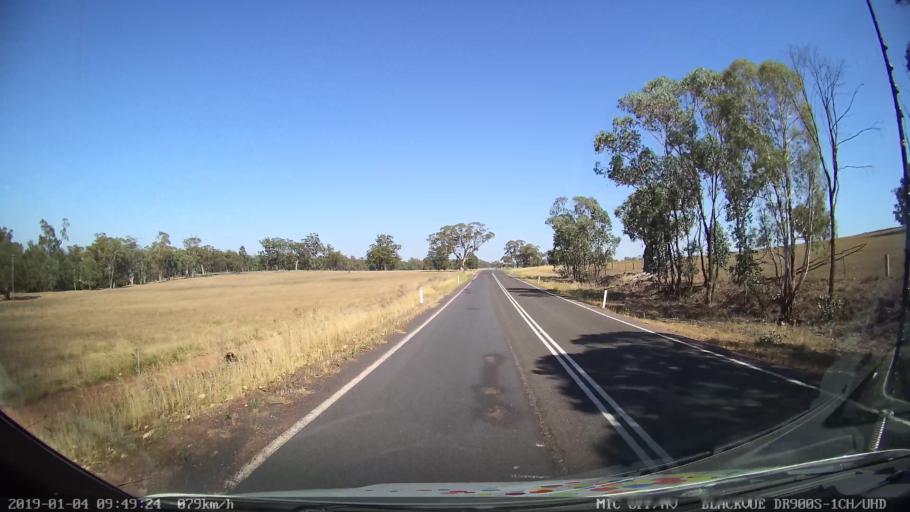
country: AU
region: New South Wales
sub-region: Cabonne
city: Canowindra
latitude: -33.5952
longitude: 148.4198
